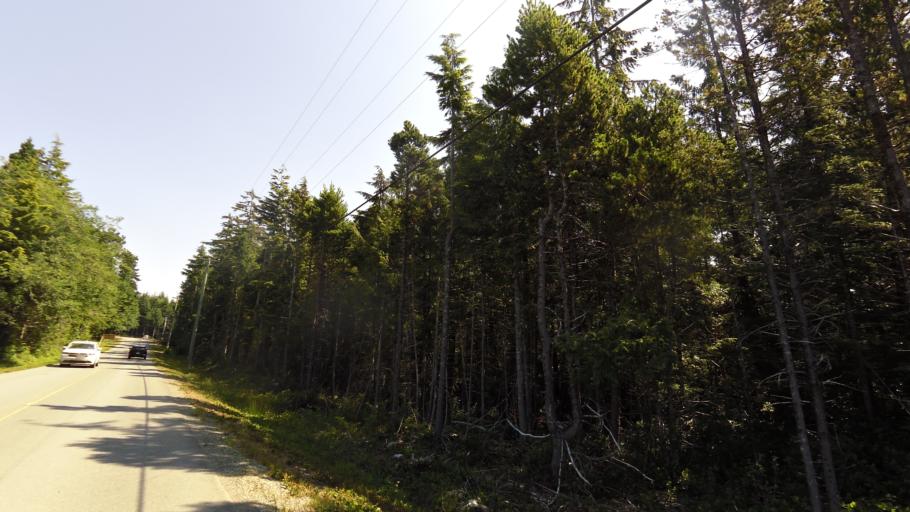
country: CA
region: British Columbia
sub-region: Regional District of Alberni-Clayoquot
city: Ucluelet
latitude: 49.0186
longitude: -125.6397
